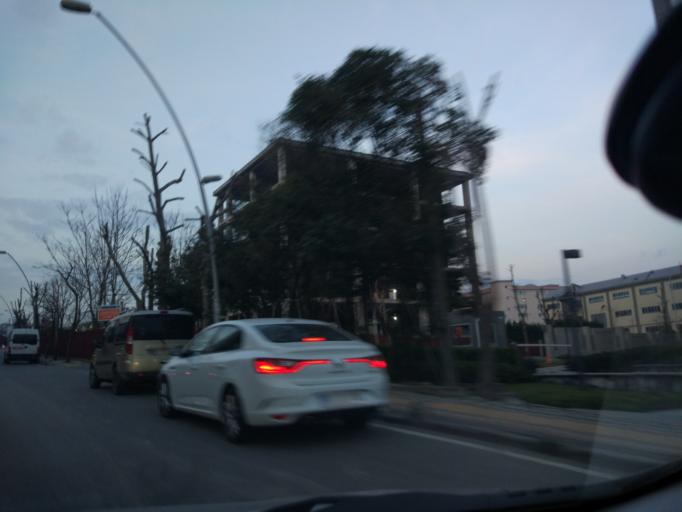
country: TR
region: Istanbul
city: Bahcelievler
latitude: 41.0024
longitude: 28.8220
